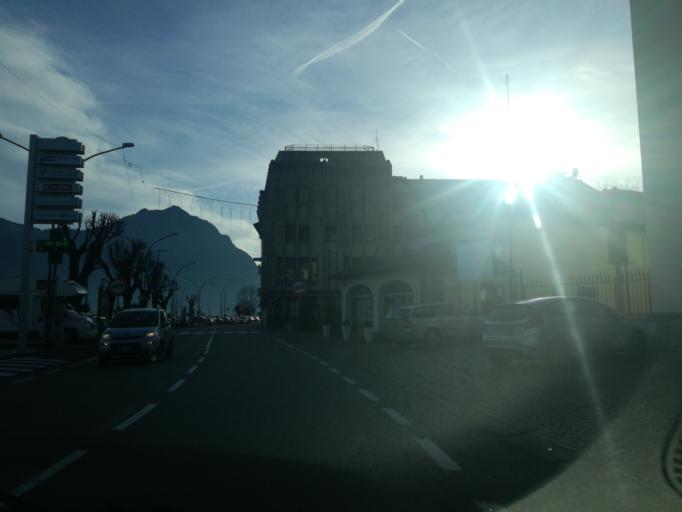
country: IT
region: Lombardy
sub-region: Provincia di Bergamo
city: Lovere
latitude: 45.8212
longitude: 10.0793
